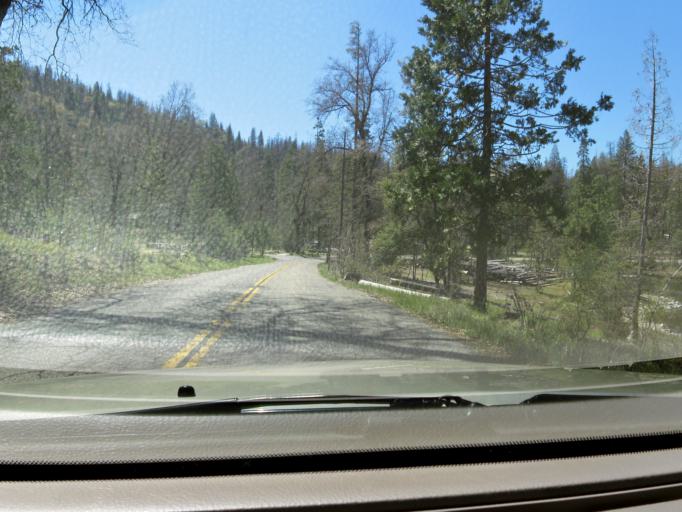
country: US
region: California
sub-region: Madera County
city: Oakhurst
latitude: 37.3136
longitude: -119.5692
